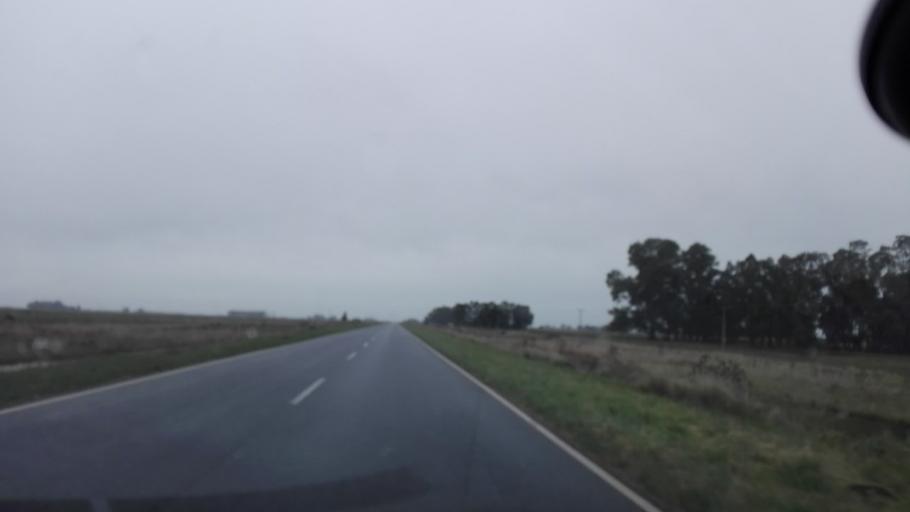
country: AR
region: Buenos Aires
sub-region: Partido de Rauch
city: Rauch
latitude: -36.9173
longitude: -58.9861
